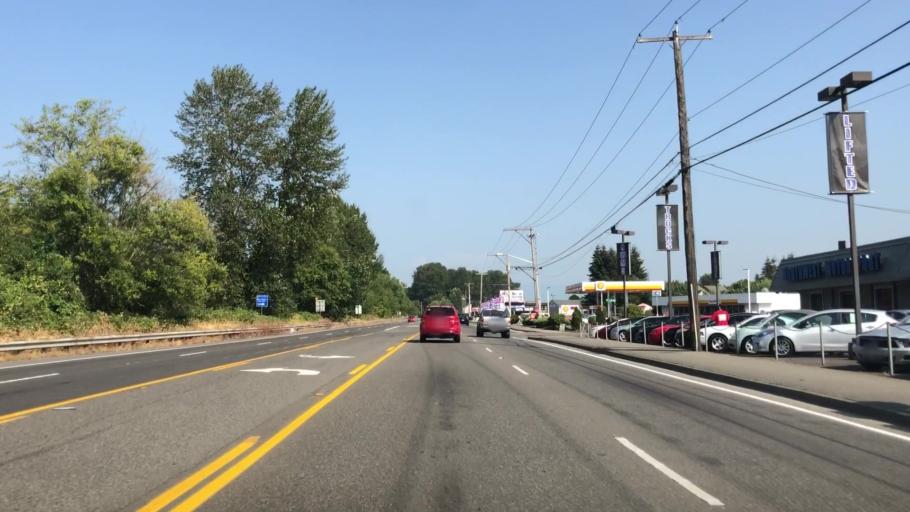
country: US
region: Washington
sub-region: Pierce County
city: Puyallup
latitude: 47.2062
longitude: -122.3198
